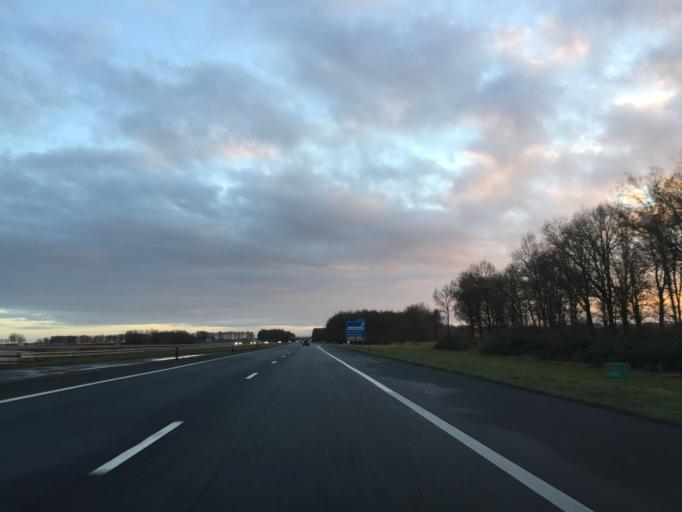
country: NL
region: Flevoland
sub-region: Gemeente Noordoostpolder
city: Emmeloord
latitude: 52.7341
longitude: 5.7692
